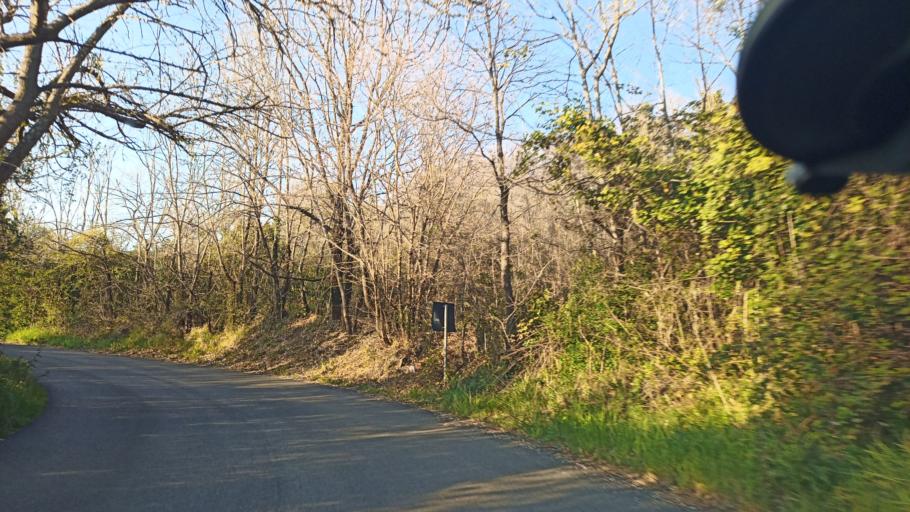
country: IT
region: Latium
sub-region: Provincia di Rieti
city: Roccantica
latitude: 42.3209
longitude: 12.6826
